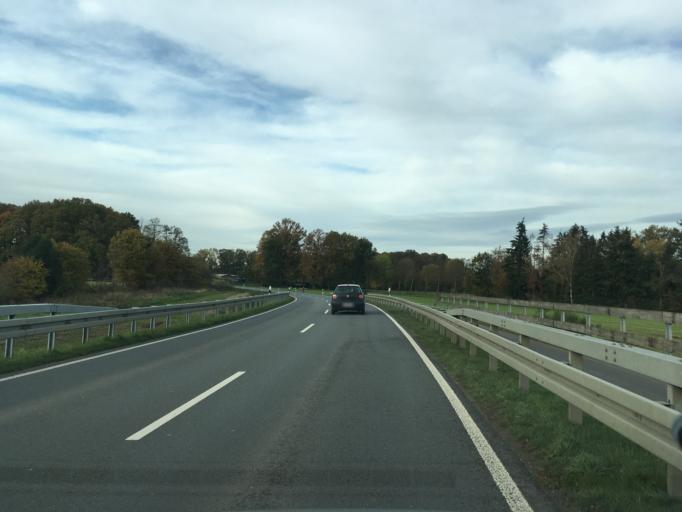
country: DE
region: North Rhine-Westphalia
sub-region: Regierungsbezirk Munster
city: Heiden
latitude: 51.8812
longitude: 6.9091
